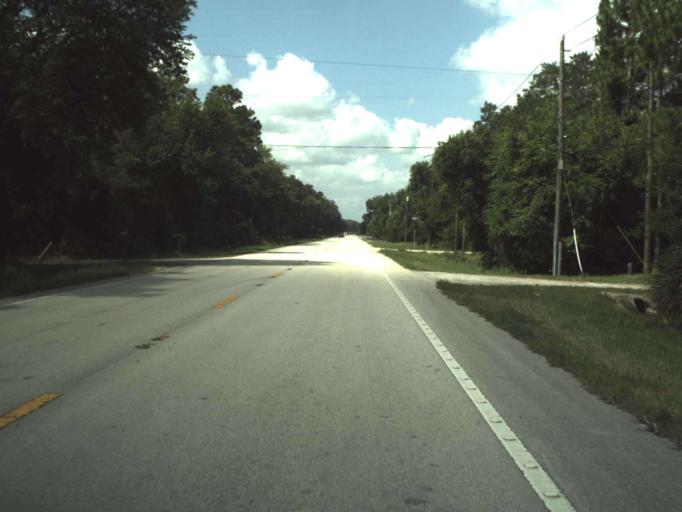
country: US
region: Florida
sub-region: Volusia County
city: Samsula-Spruce Creek
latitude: 28.9350
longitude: -81.1082
